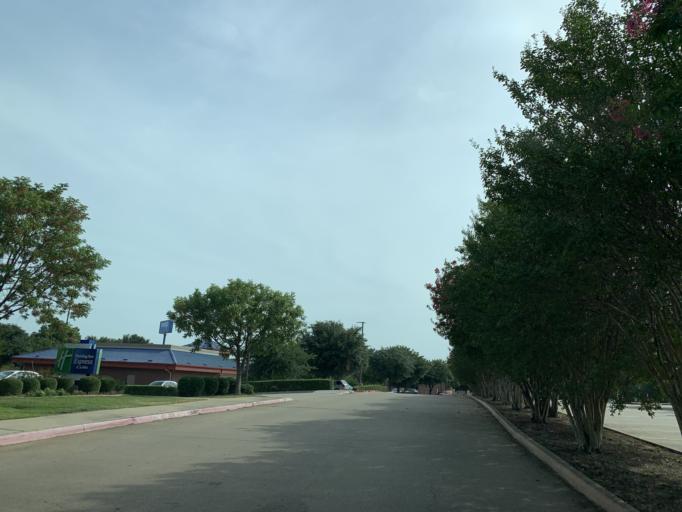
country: US
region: Texas
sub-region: Dallas County
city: Grand Prairie
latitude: 32.6734
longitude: -97.0099
